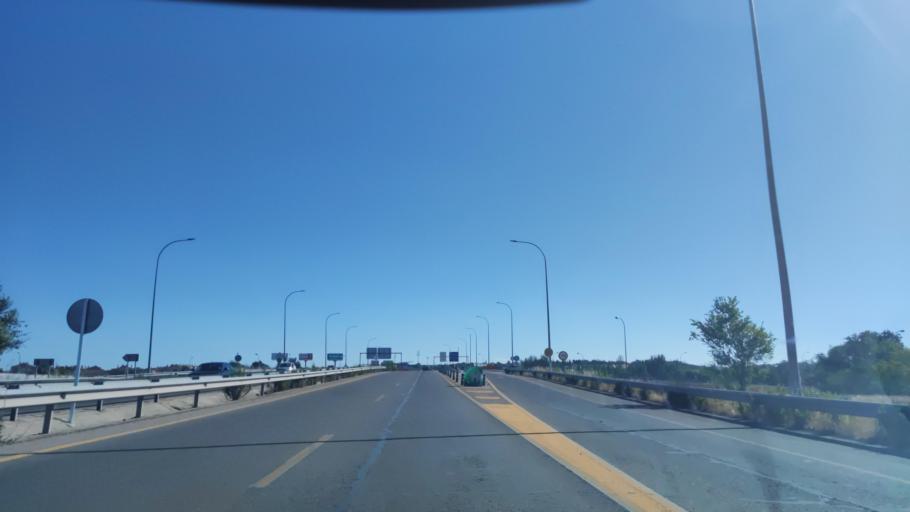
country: ES
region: Madrid
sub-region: Provincia de Madrid
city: Leganes
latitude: 40.3539
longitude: -3.7507
